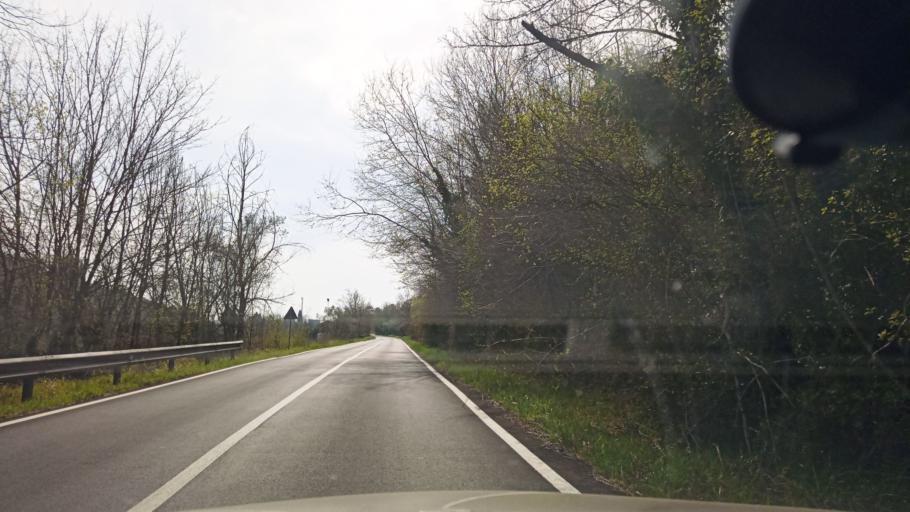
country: IT
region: Latium
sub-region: Provincia di Rieti
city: Cantalupo in Sabina
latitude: 42.3147
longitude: 12.6442
